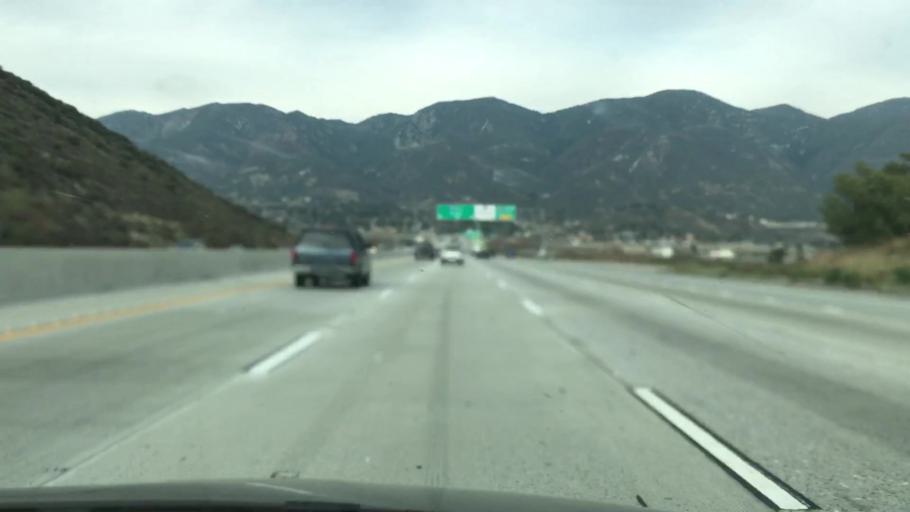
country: US
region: California
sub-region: San Bernardino County
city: Muscoy
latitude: 34.2090
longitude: -117.4129
